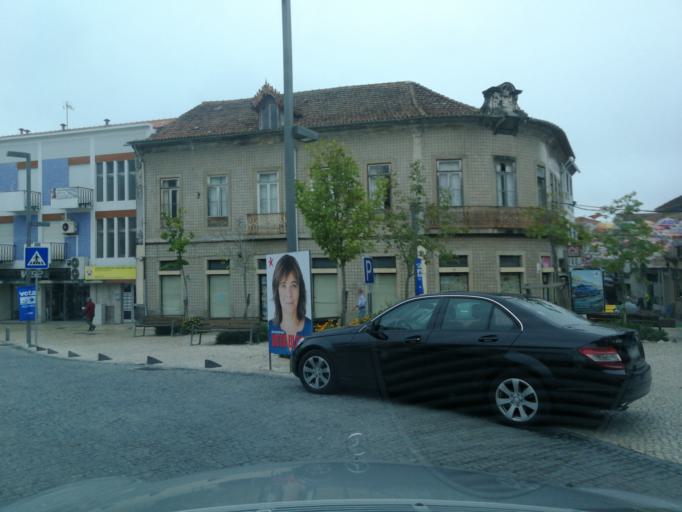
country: PT
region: Aveiro
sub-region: Agueda
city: Agueda
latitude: 40.5728
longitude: -8.4459
